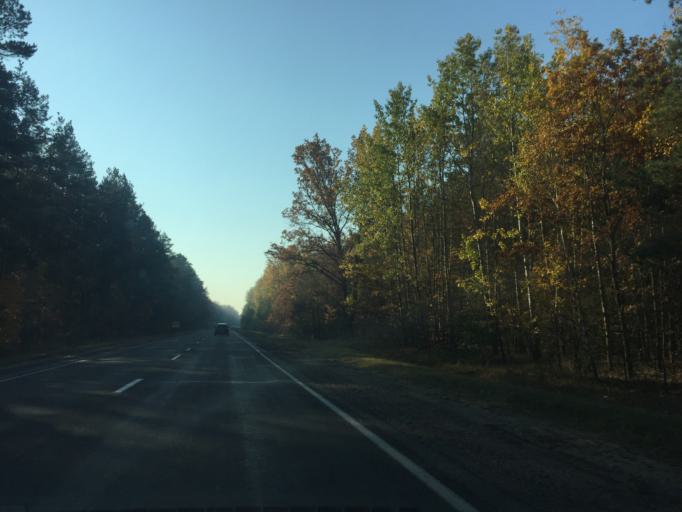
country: BY
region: Gomel
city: Gomel
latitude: 52.4060
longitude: 30.8289
